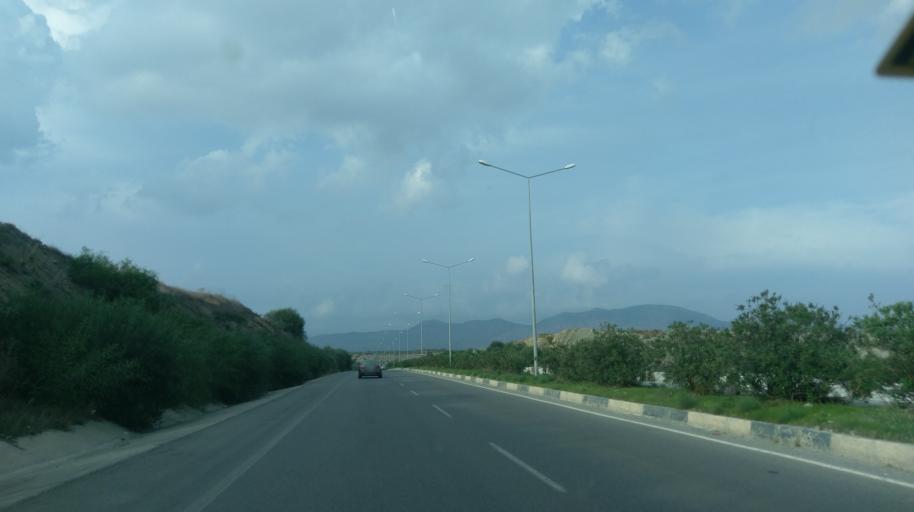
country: CY
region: Lefkosia
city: Nicosia
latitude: 35.2314
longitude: 33.3120
